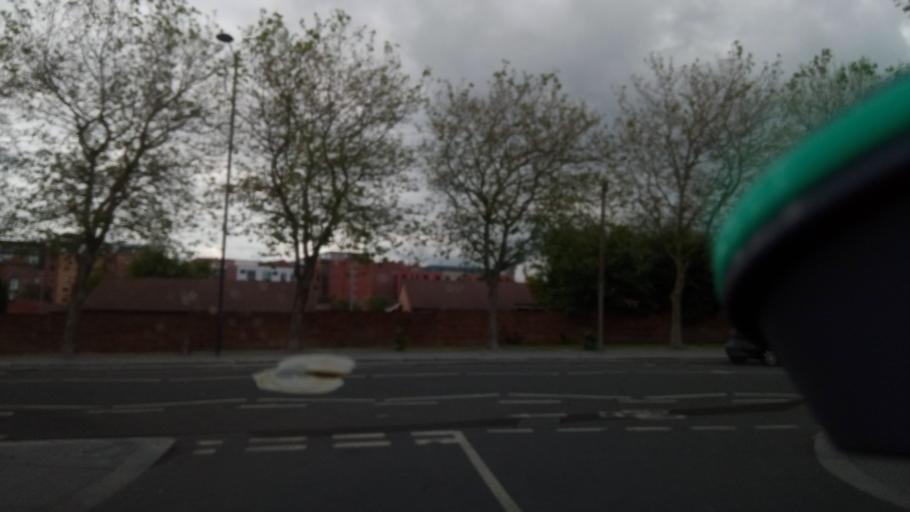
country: GB
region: England
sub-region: Liverpool
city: Liverpool
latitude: 53.3994
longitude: -2.9840
